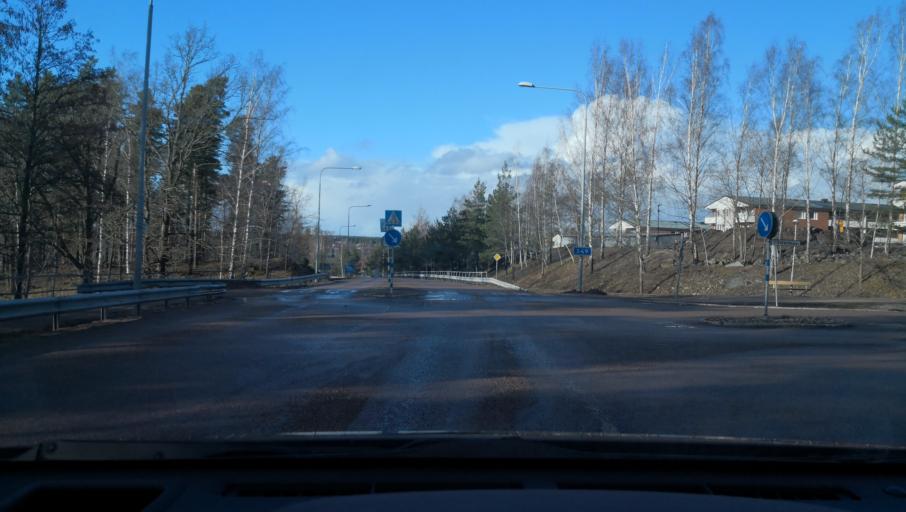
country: SE
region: Vaestmanland
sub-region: Arboga Kommun
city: Arboga
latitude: 59.3846
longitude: 15.8390
